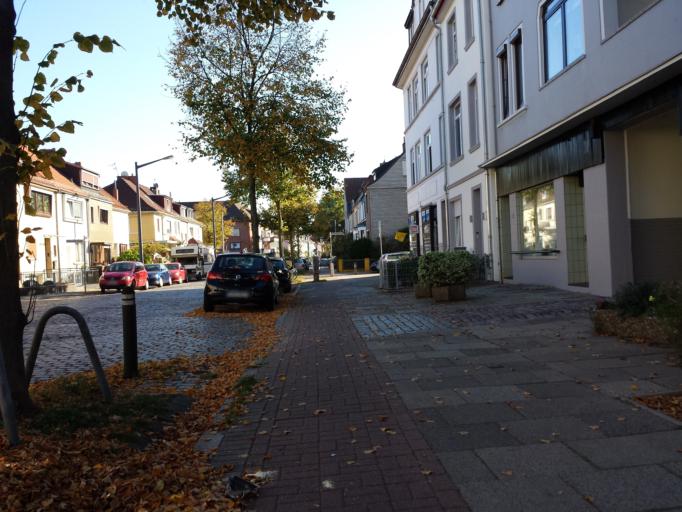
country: DE
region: Bremen
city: Bremen
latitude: 53.1011
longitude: 8.7784
